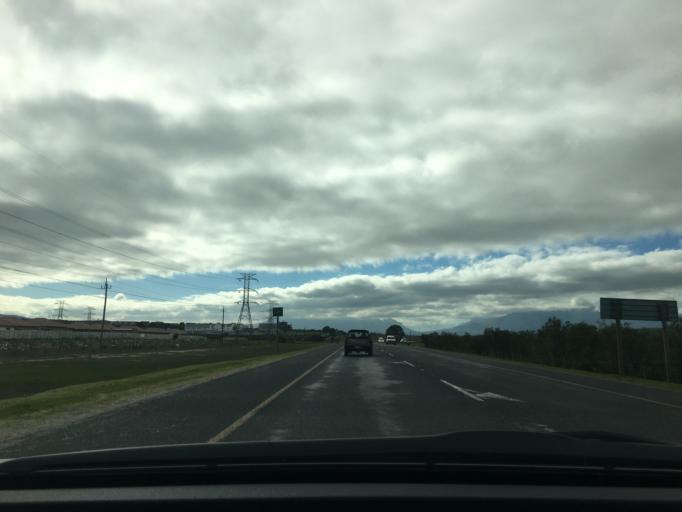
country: ZA
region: Western Cape
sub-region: Cape Winelands District Municipality
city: Stellenbosch
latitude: -34.0250
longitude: 18.7374
